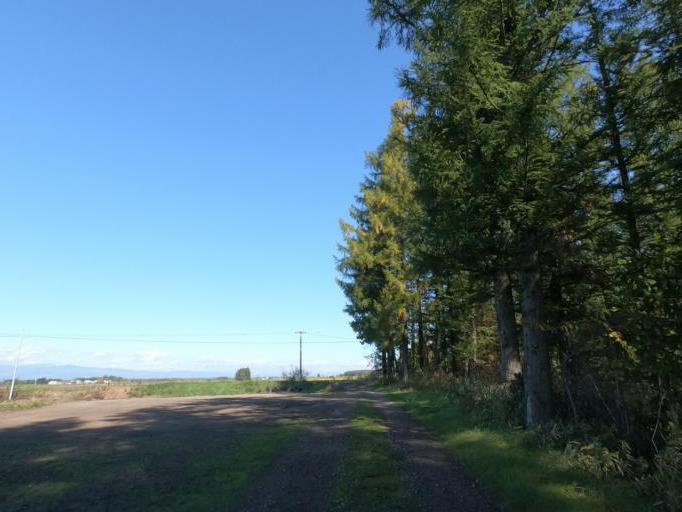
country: JP
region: Hokkaido
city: Otofuke
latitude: 43.0166
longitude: 143.2700
